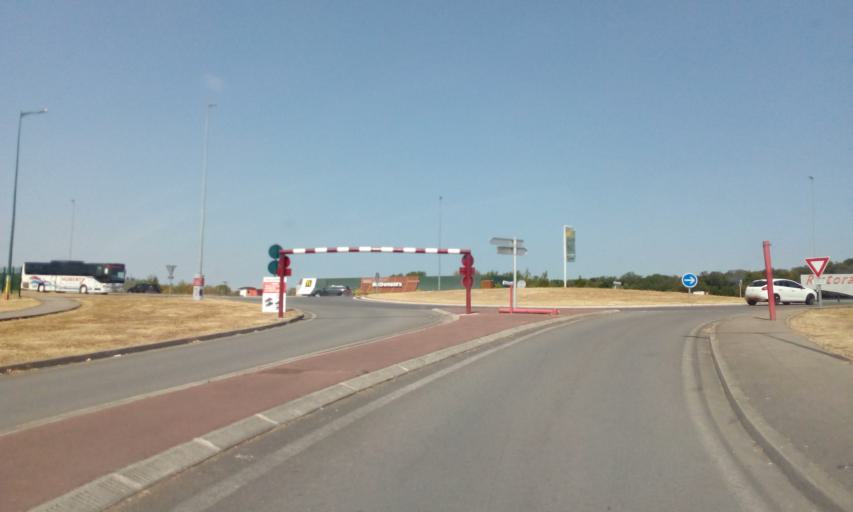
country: FR
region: Lorraine
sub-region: Departement de Meurthe-et-Moselle
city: Longlaville
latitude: 49.5467
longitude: 5.8071
